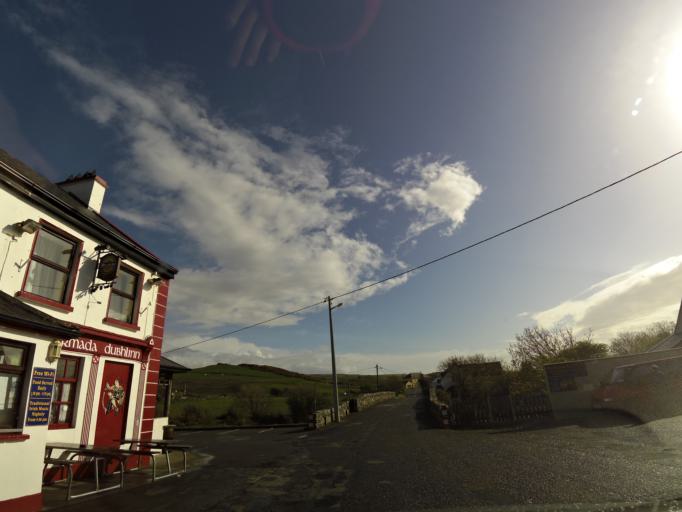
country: IE
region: Connaught
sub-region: County Galway
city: Bearna
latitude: 53.0191
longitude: -9.3713
